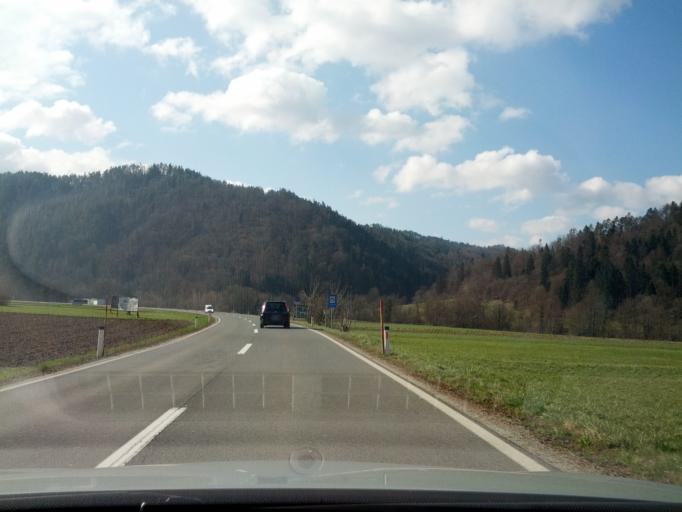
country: SI
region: Litija
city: Litija
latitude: 46.0651
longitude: 14.8158
